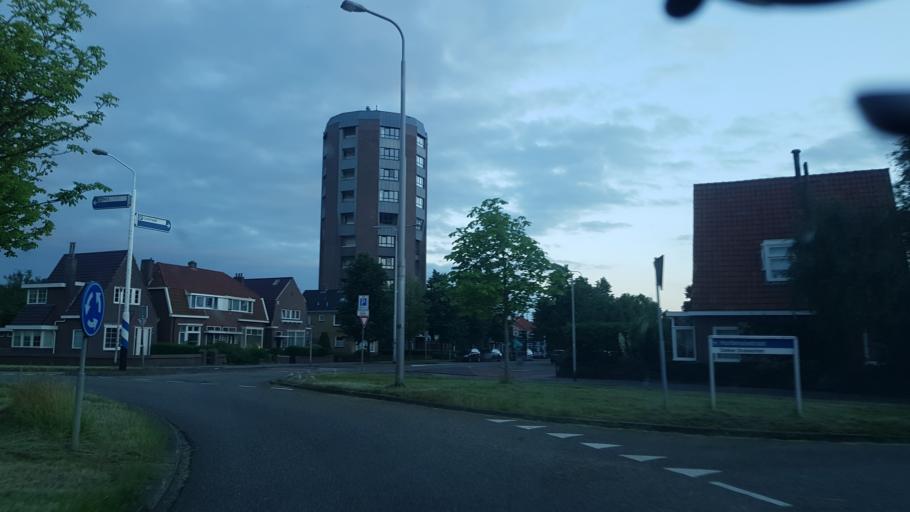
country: NL
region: Friesland
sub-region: Gemeente Leeuwarden
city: Leeuwarden
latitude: 53.2123
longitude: 5.8138
